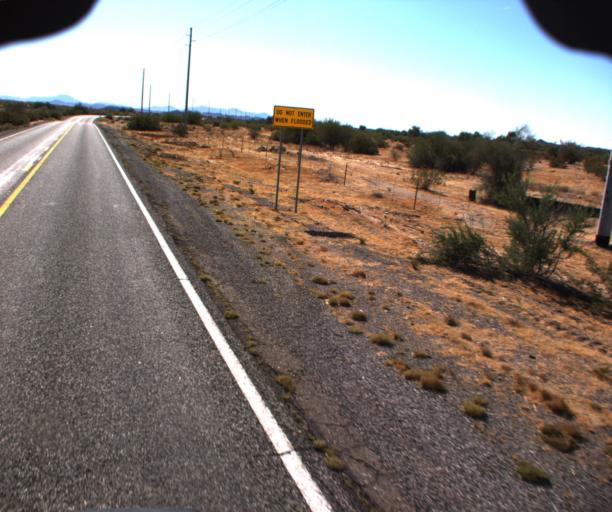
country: US
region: Arizona
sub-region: La Paz County
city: Cienega Springs
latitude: 33.9917
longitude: -114.0830
